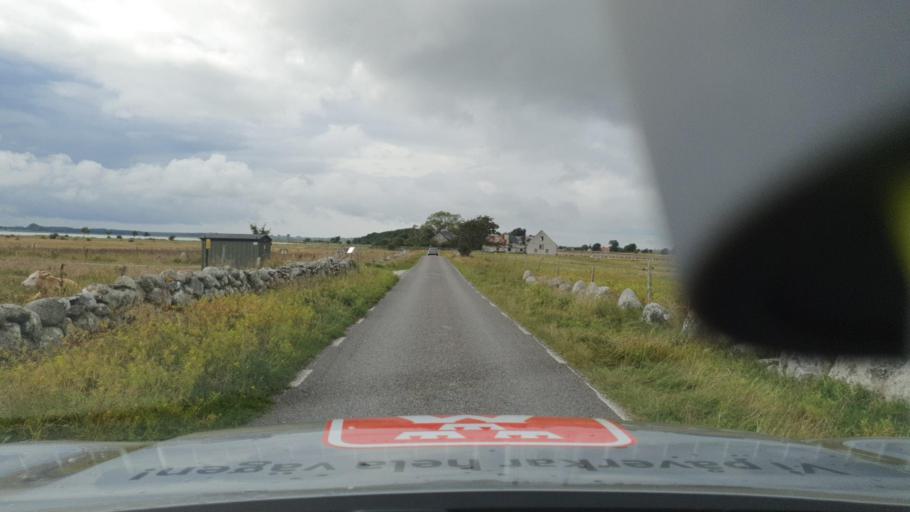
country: SE
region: Gotland
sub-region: Gotland
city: Hemse
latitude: 56.9966
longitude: 18.3884
